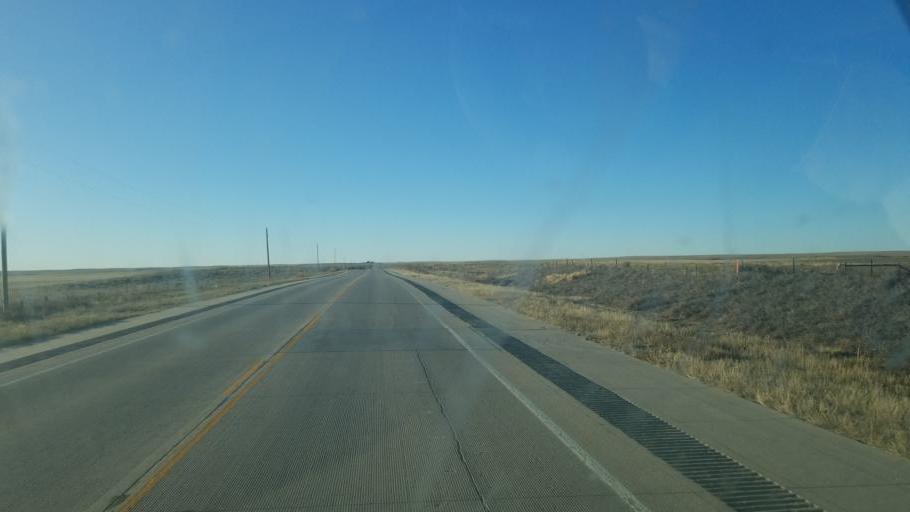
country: US
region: Colorado
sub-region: Kiowa County
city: Eads
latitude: 38.6293
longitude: -102.7860
